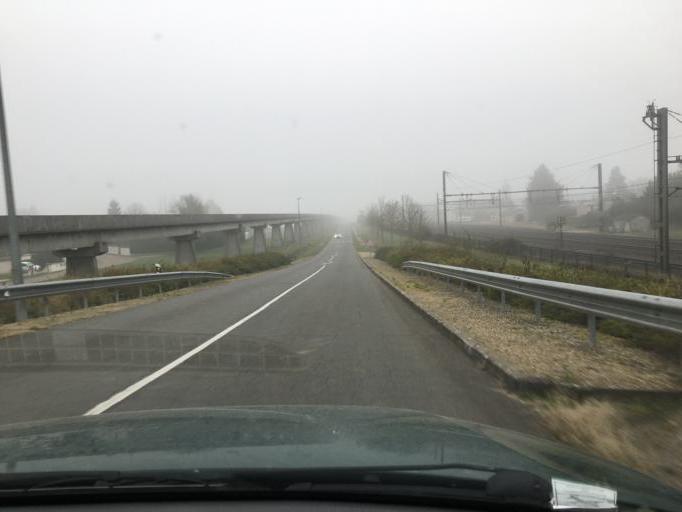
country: FR
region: Centre
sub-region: Departement du Loiret
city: Saran
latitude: 47.9893
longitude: 1.8845
